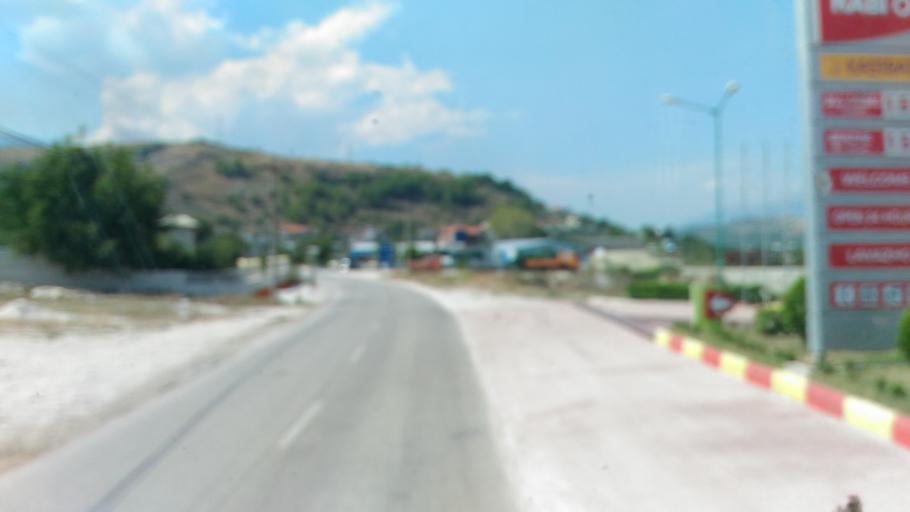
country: AL
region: Gjirokaster
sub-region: Rrethi i Gjirokastres
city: Dervician
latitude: 40.0553
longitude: 20.1755
